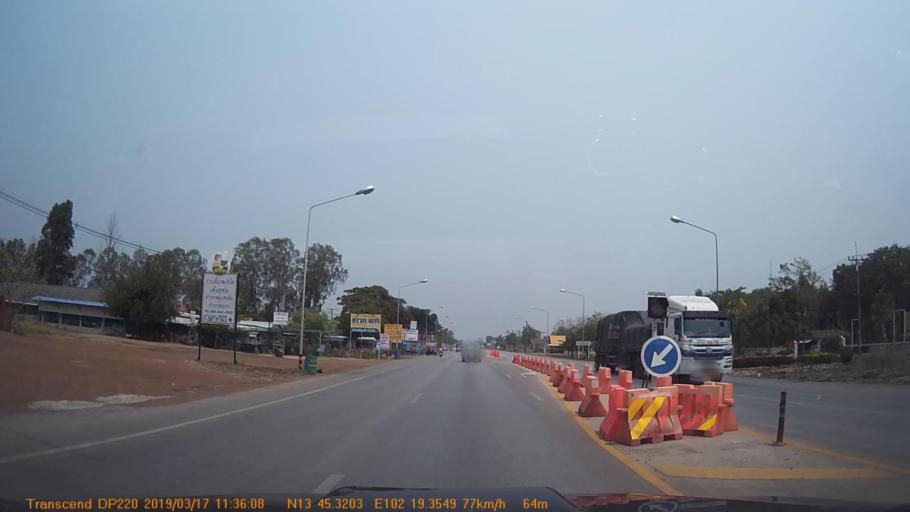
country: TH
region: Sa Kaeo
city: Watthana Nakhon
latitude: 13.7556
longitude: 102.3227
